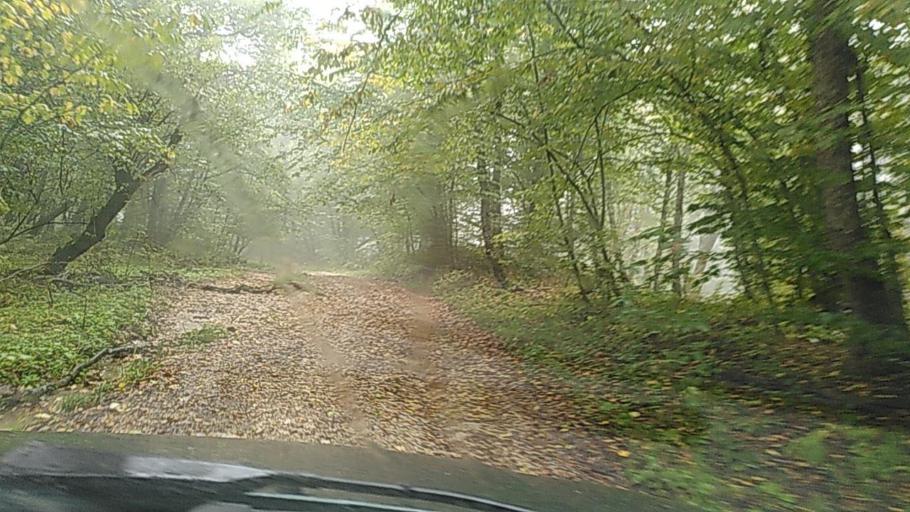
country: RU
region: Kabardino-Balkariya
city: Belaya Rechka
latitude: 43.3612
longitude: 43.4139
